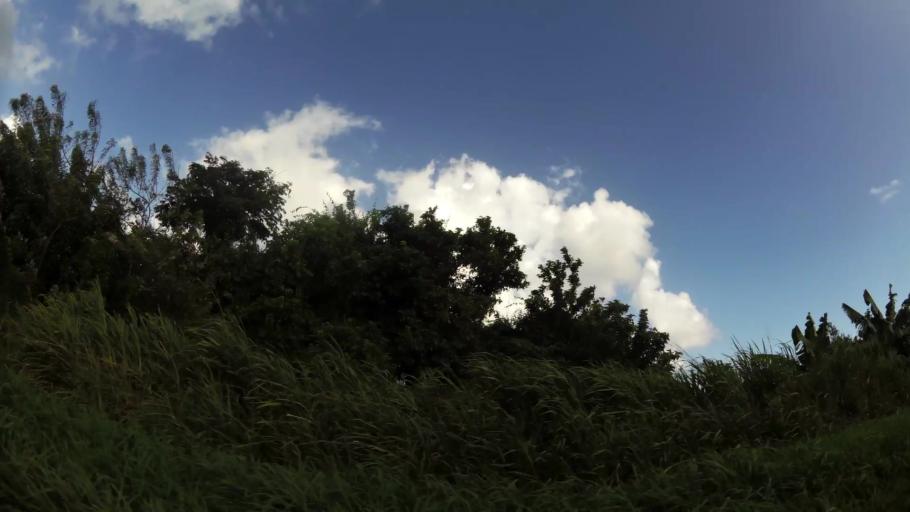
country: MQ
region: Martinique
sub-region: Martinique
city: Le Lorrain
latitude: 14.8279
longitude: -61.0353
